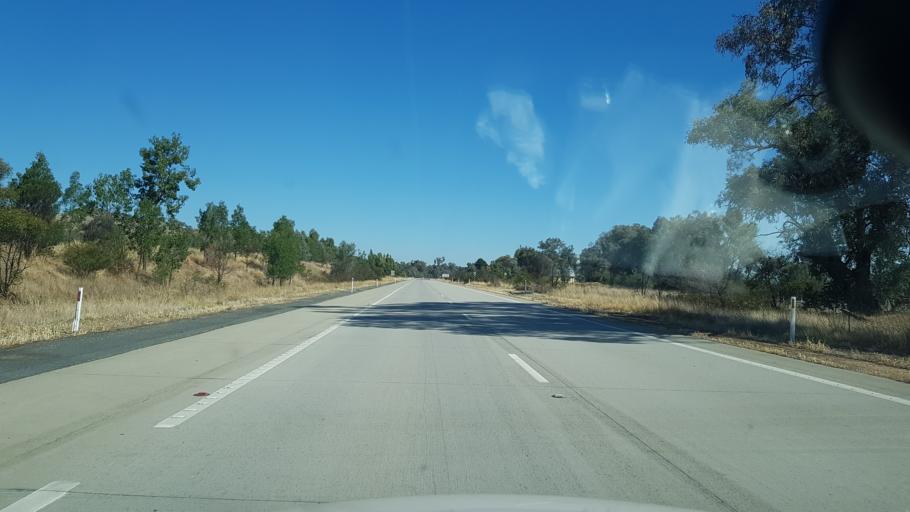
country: AU
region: New South Wales
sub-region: Greater Hume Shire
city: Holbrook
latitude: -35.8968
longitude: 147.1674
